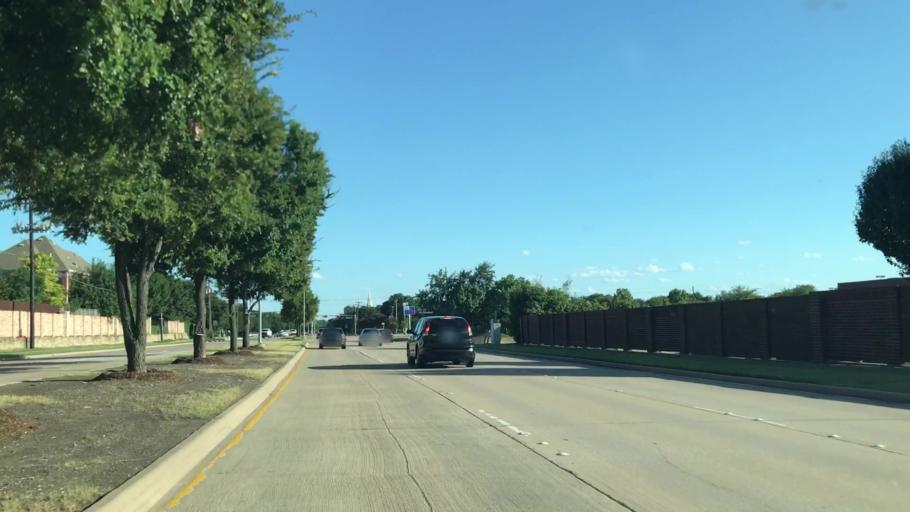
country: US
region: Texas
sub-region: Collin County
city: Plano
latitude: 33.0737
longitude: -96.7369
